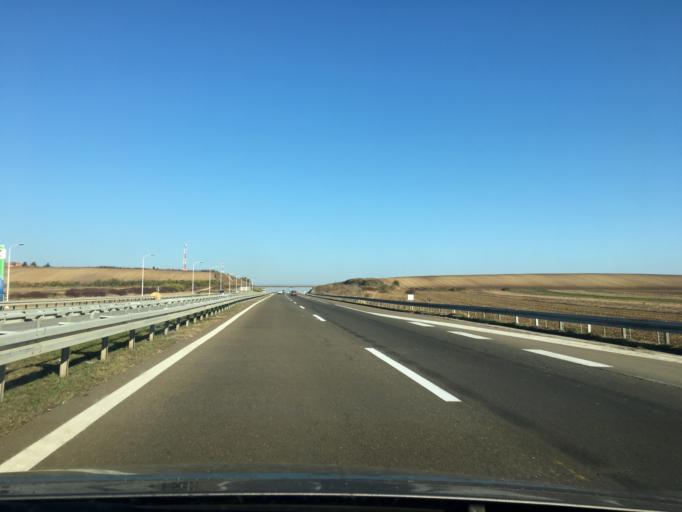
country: RS
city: Beska
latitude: 45.1499
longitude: 20.0831
